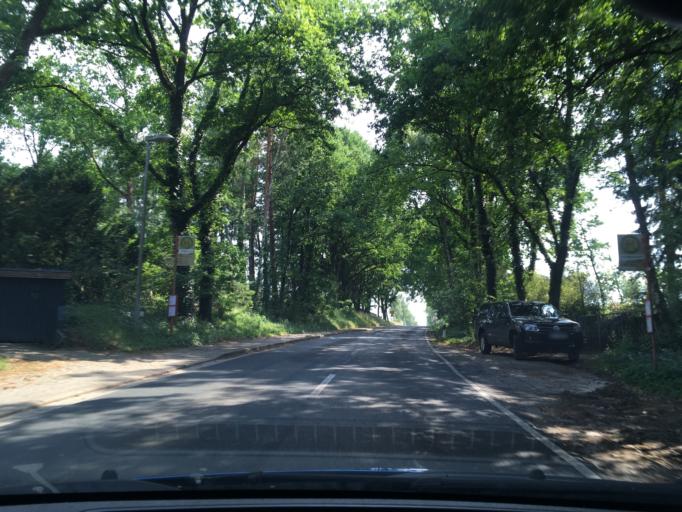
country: DE
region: Lower Saxony
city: Jesteburg
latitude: 53.2775
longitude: 9.9141
